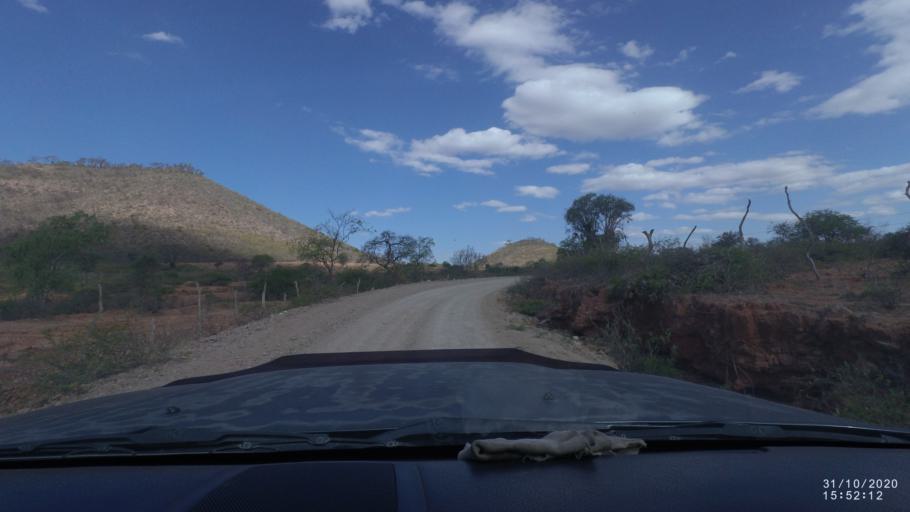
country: BO
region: Chuquisaca
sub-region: Provincia Zudanez
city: Mojocoya
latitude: -18.3180
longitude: -64.6955
